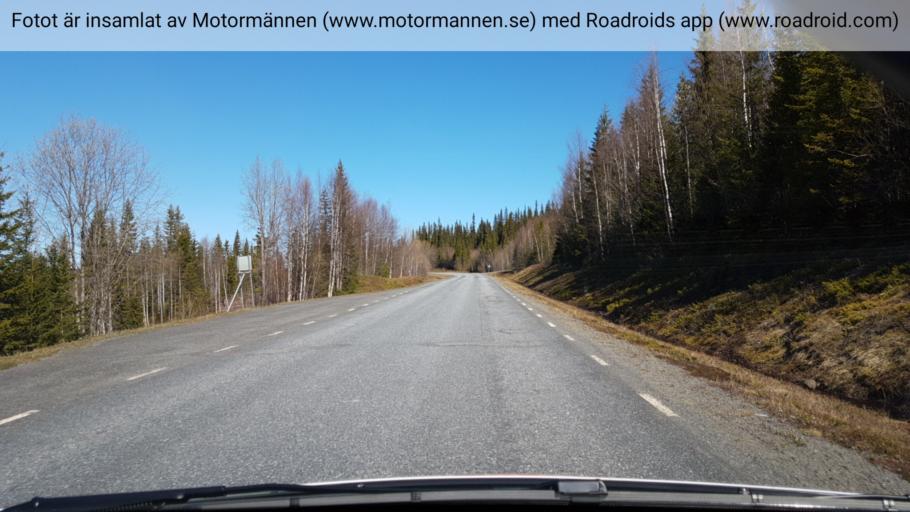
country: SE
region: Vaesterbotten
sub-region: Vilhelmina Kommun
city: Sjoberg
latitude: 64.9664
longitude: 15.8594
